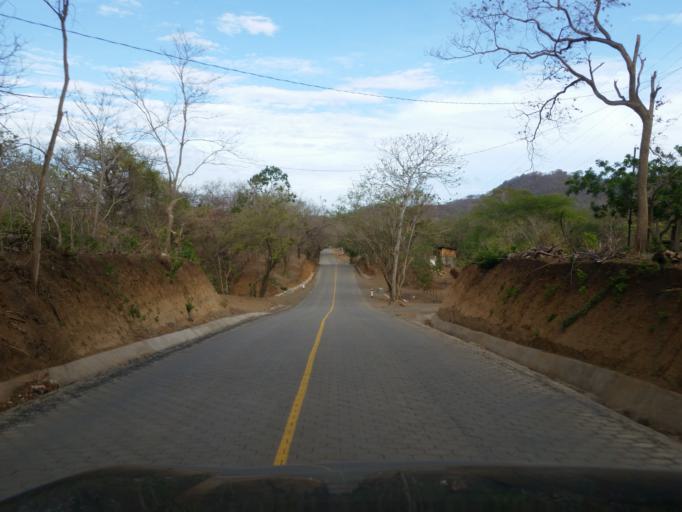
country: NI
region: Rivas
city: Tola
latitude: 11.3990
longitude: -85.9938
